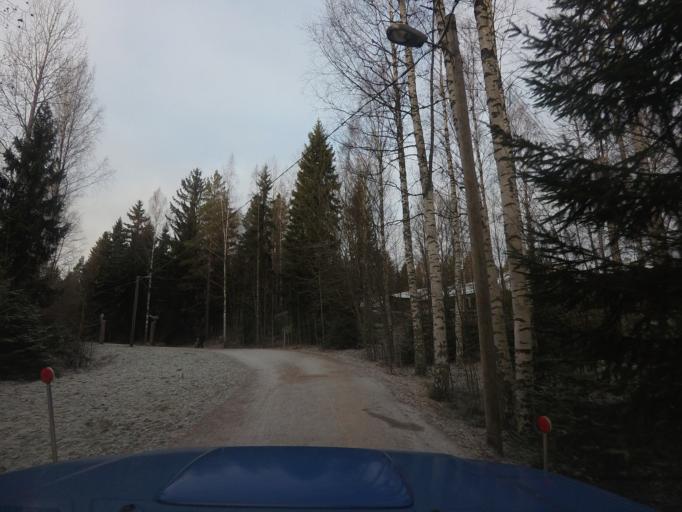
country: FI
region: Uusimaa
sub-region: Helsinki
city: Espoo
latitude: 60.1920
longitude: 24.6834
